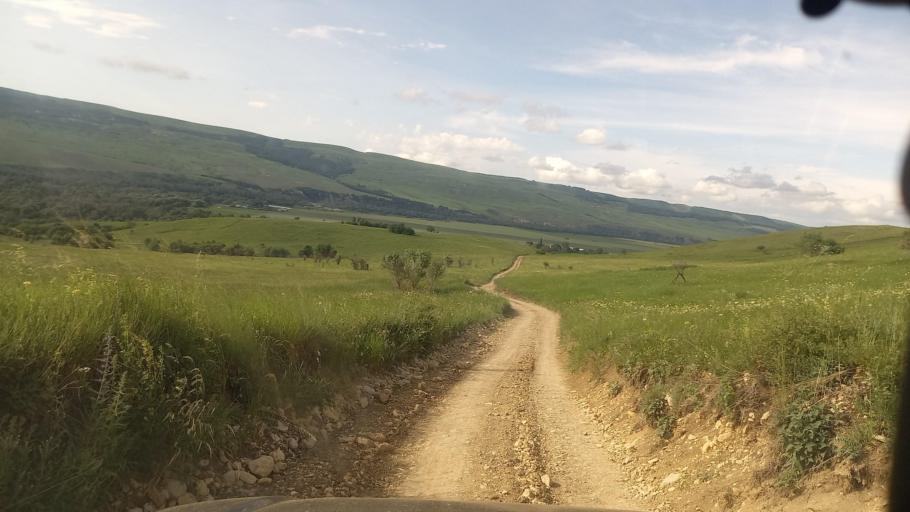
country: RU
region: Krasnodarskiy
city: Peredovaya
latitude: 44.0761
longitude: 41.3635
